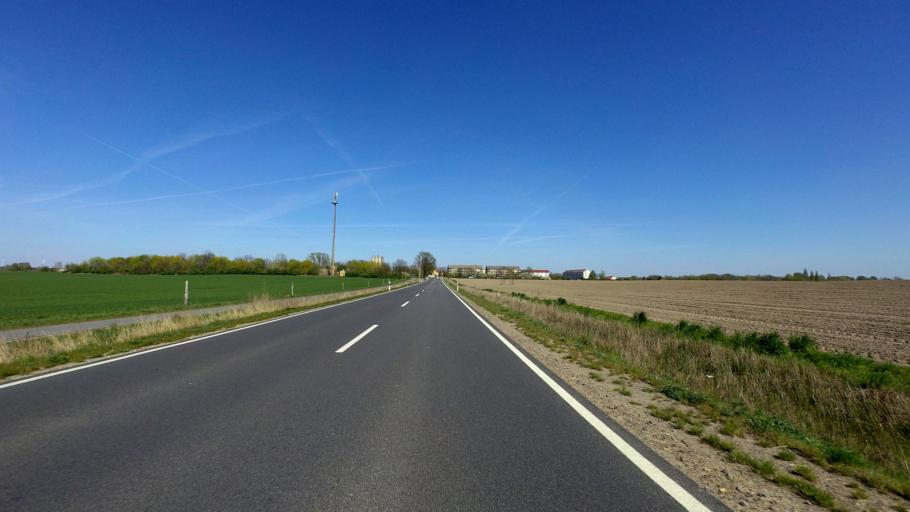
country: DE
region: Saxony-Anhalt
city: Kalbe
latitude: 52.6542
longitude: 11.3692
